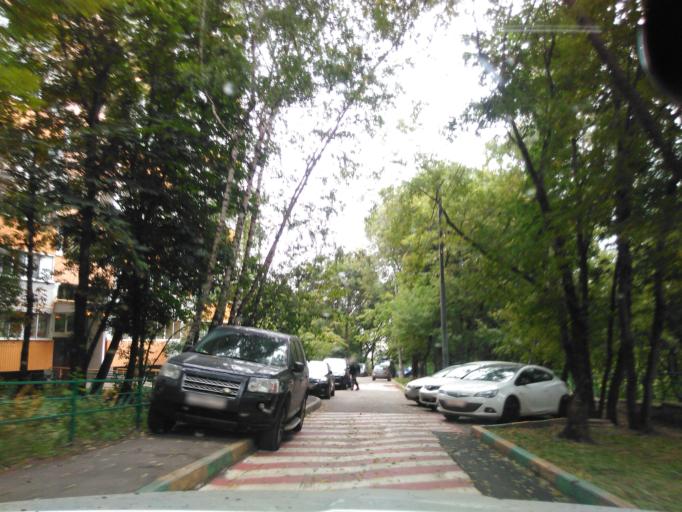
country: RU
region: Moskovskaya
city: Bol'shaya Setun'
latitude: 55.7219
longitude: 37.4139
